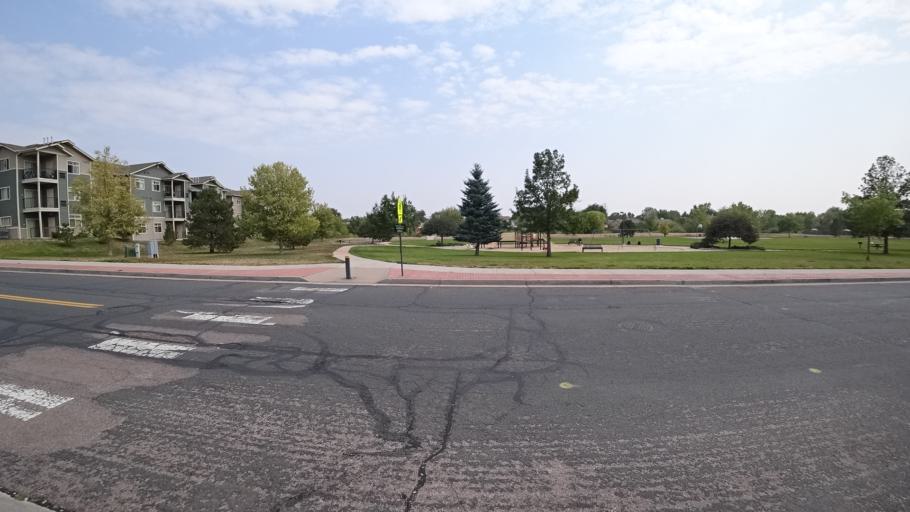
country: US
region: Colorado
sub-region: El Paso County
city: Cimarron Hills
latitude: 38.8228
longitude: -104.7446
